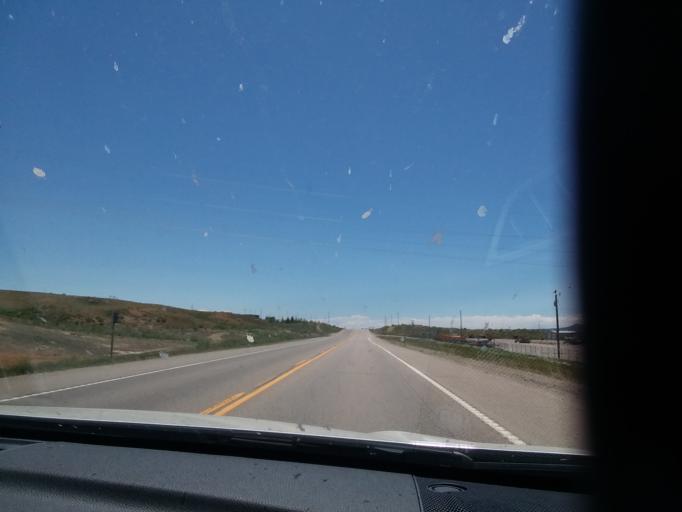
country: US
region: Wyoming
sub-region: Sweetwater County
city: North Rock Springs
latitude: 41.6331
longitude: -109.2308
